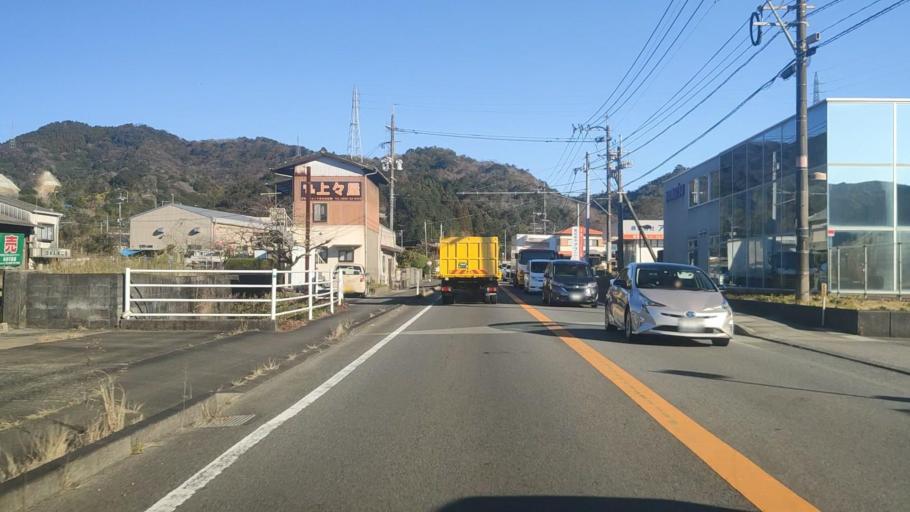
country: JP
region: Miyazaki
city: Nobeoka
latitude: 32.4993
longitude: 131.6630
